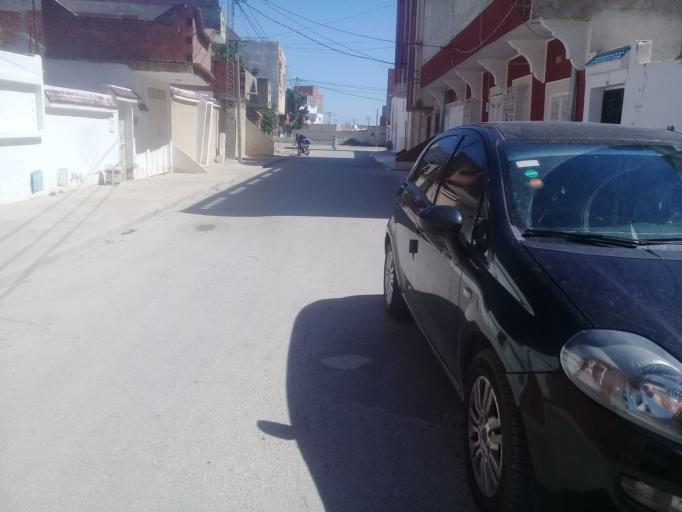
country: TN
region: Al Qayrawan
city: Kairouan
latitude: 35.6610
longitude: 10.1073
